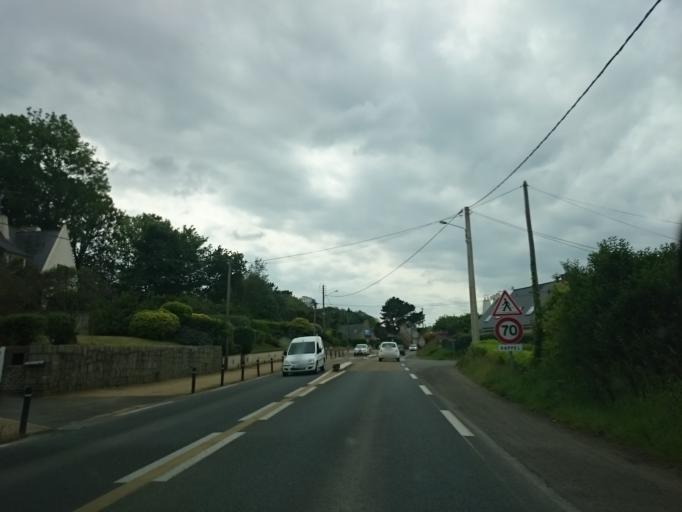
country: FR
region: Brittany
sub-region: Departement des Cotes-d'Armor
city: Louannec
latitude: 48.7960
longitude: -3.4245
